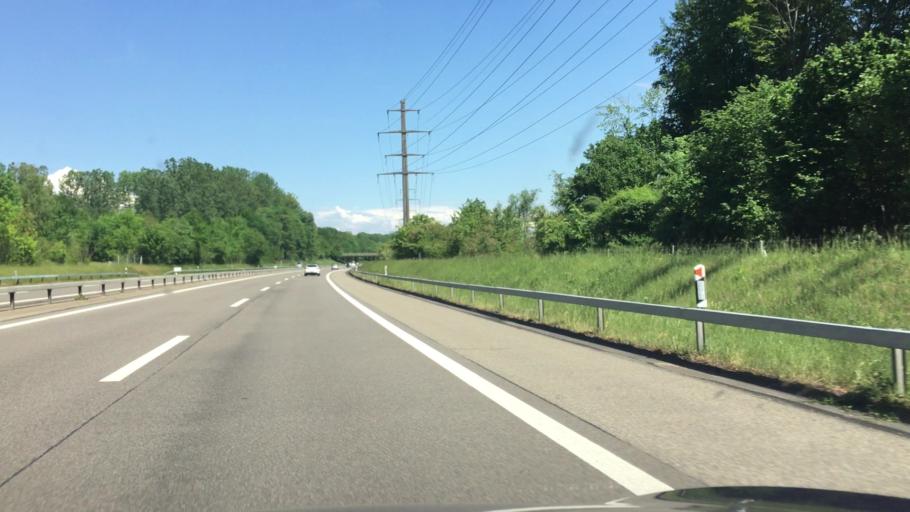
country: CH
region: Thurgau
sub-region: Frauenfeld District
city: Pfyn
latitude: 47.5861
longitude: 8.9411
